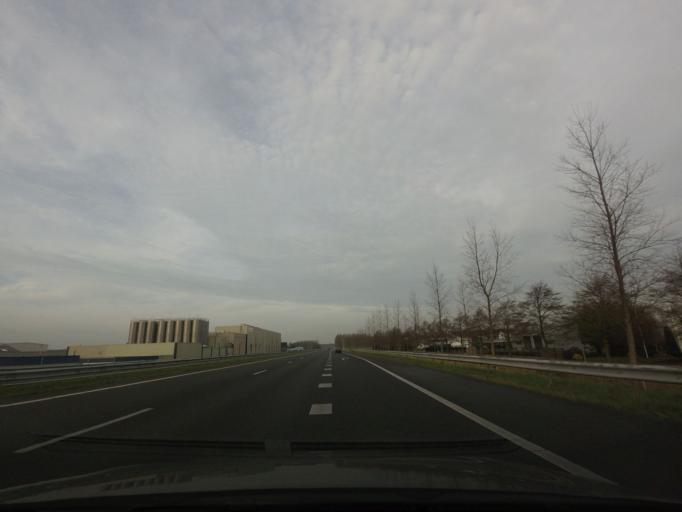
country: NL
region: North Holland
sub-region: Gemeente Medemblik
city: Opperdoes
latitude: 52.8362
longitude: 5.0211
